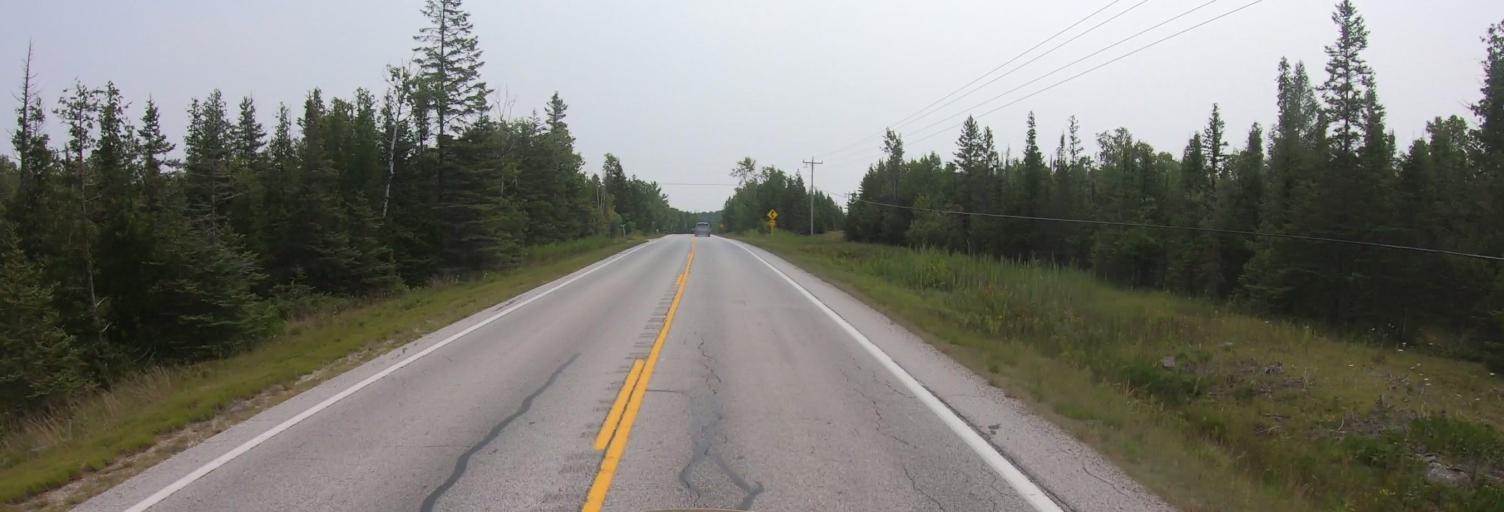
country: CA
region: Ontario
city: Thessalon
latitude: 45.9855
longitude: -83.8126
